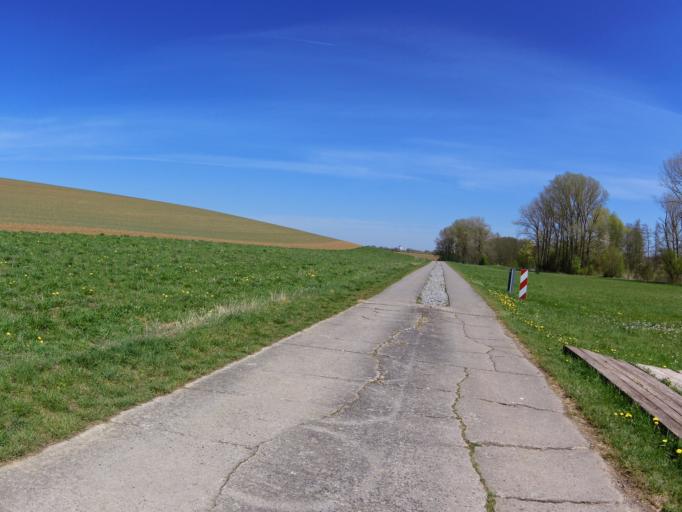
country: DE
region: Bavaria
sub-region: Regierungsbezirk Unterfranken
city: Kurnach
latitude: 49.8607
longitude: 10.0212
